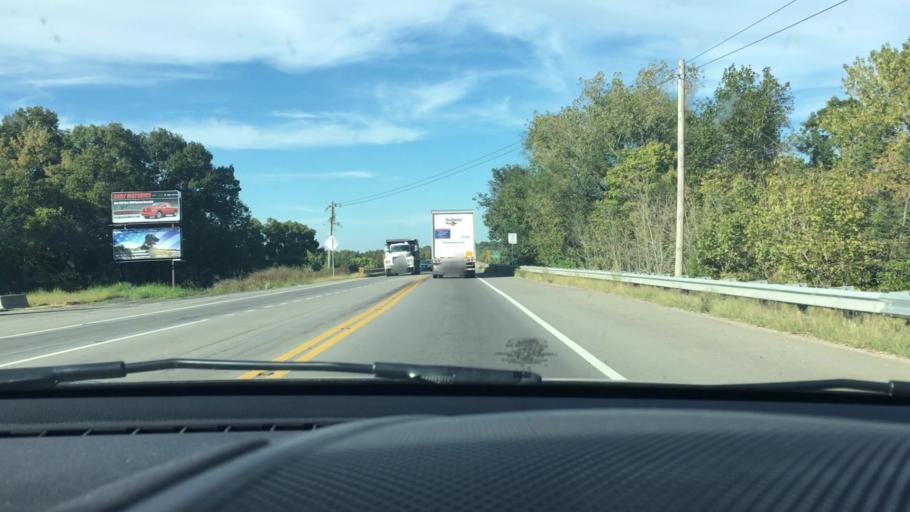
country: US
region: Tennessee
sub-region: Montgomery County
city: Clarksville
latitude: 36.4792
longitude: -87.3752
